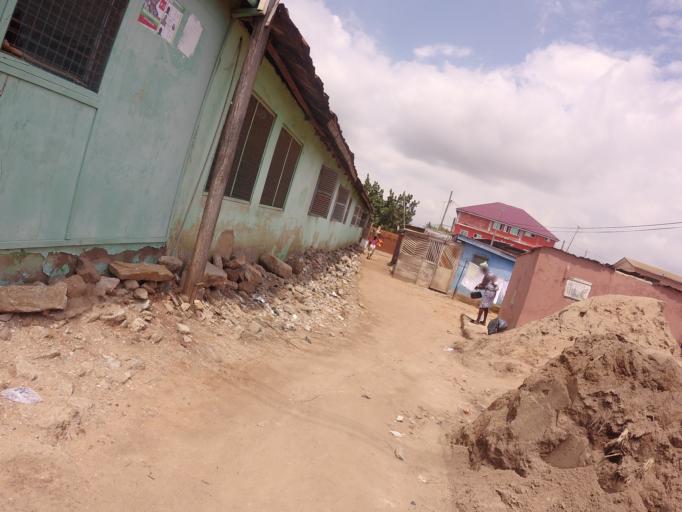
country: GH
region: Greater Accra
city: Accra
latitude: 5.5882
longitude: -0.2066
